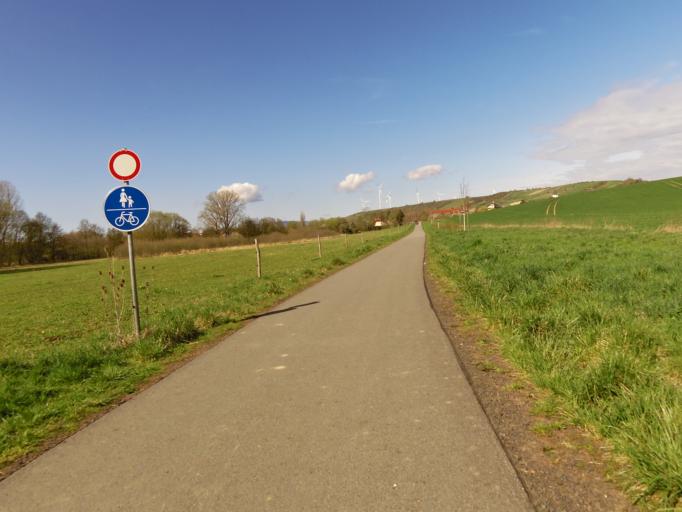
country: DE
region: Rheinland-Pfalz
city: Immesheim
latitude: 49.6476
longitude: 8.1095
